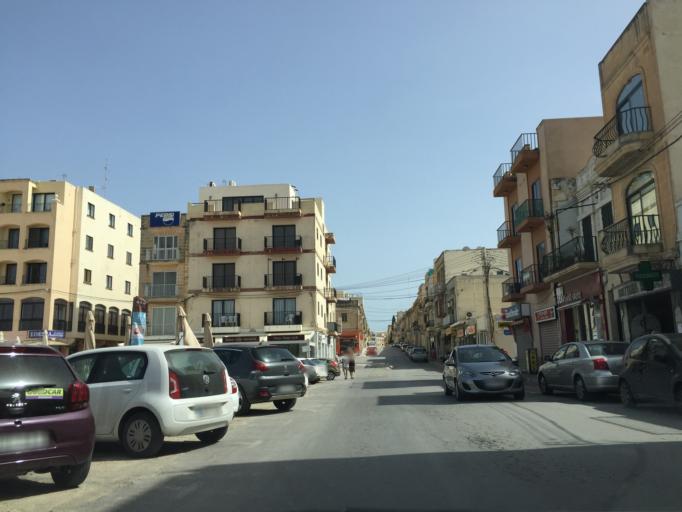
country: MT
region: Birzebbuga
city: Birzebbuga
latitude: 35.8243
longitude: 14.5283
